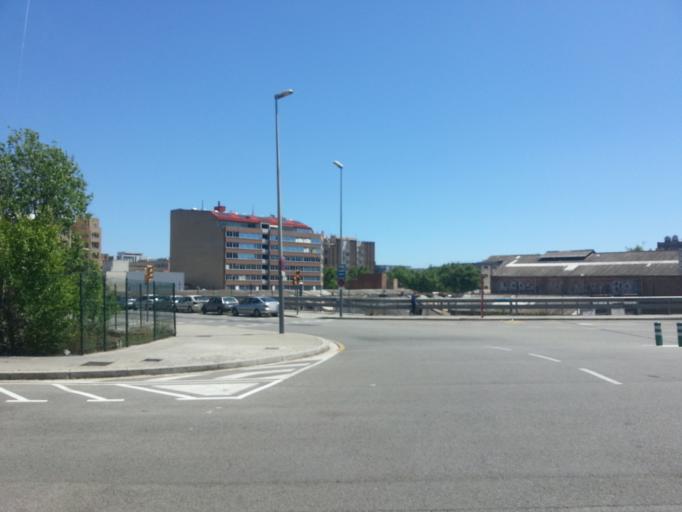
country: ES
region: Catalonia
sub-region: Provincia de Barcelona
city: Sant Marti
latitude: 41.3999
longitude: 2.1869
